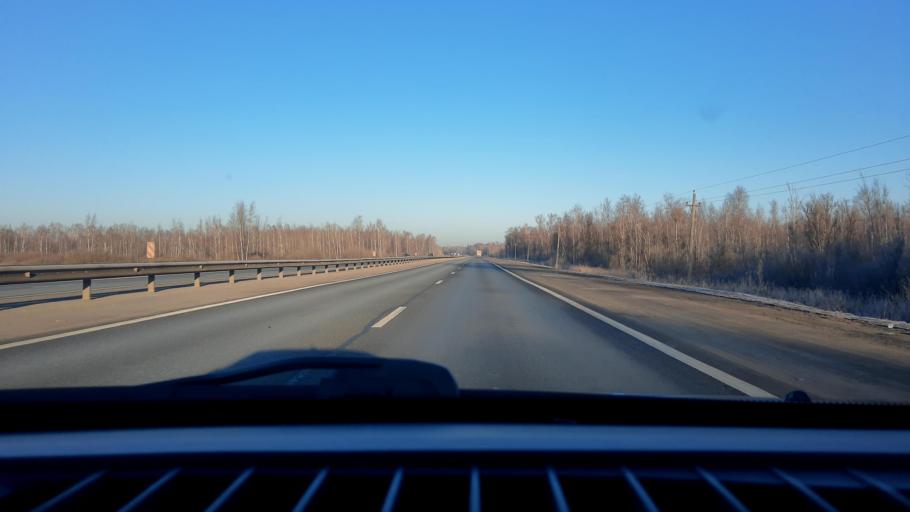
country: RU
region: Nizjnij Novgorod
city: Gorbatovka
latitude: 56.2824
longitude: 43.6995
